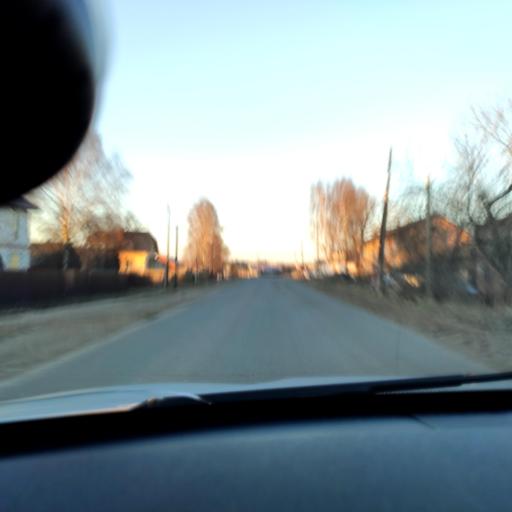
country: RU
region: Perm
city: Kultayevo
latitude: 57.9323
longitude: 55.8777
